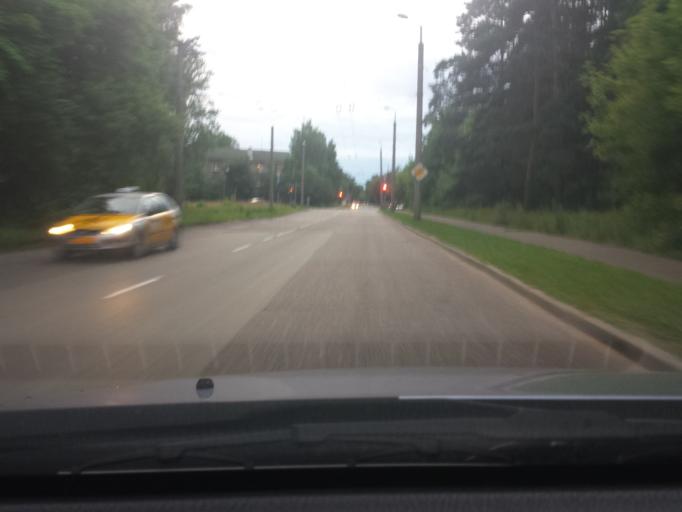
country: LV
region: Riga
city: Jaunciems
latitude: 56.9673
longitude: 24.1985
